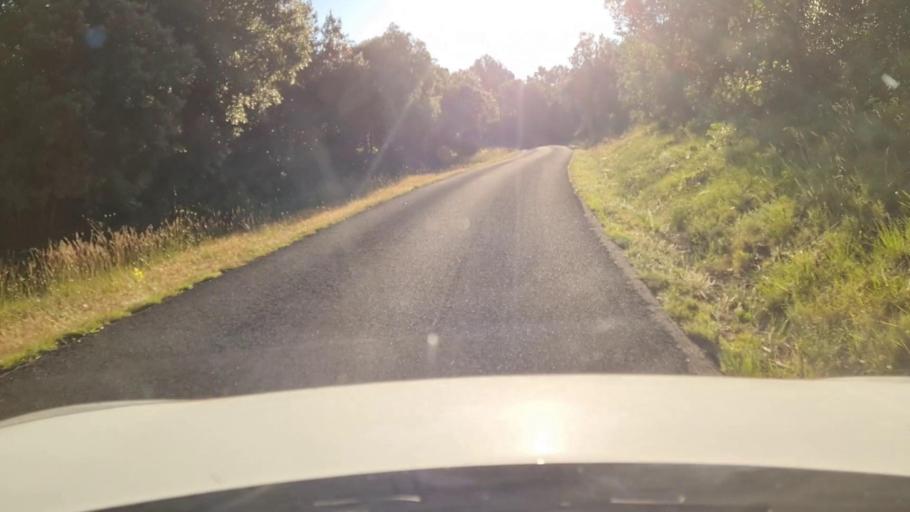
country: FR
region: Languedoc-Roussillon
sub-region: Departement du Gard
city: Calvisson
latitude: 43.8271
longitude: 4.1652
